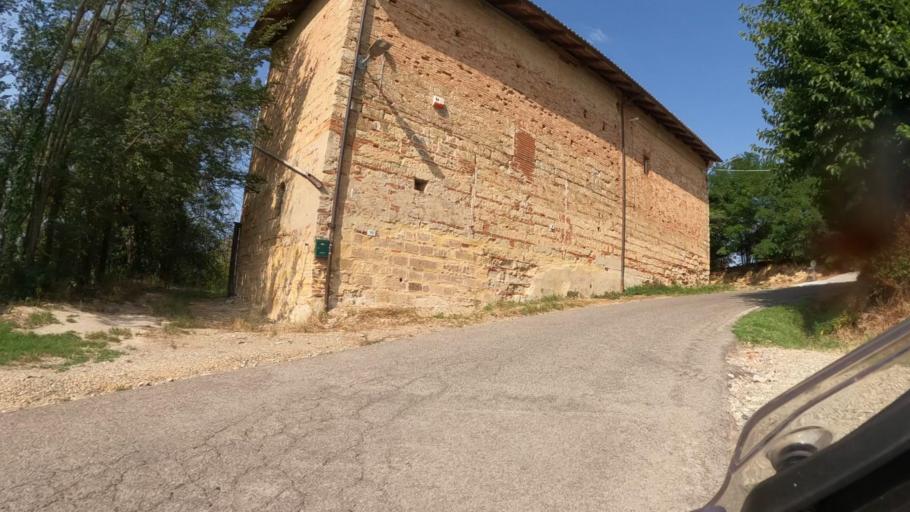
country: IT
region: Piedmont
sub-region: Provincia di Asti
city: Viarigi
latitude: 44.9542
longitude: 8.3733
